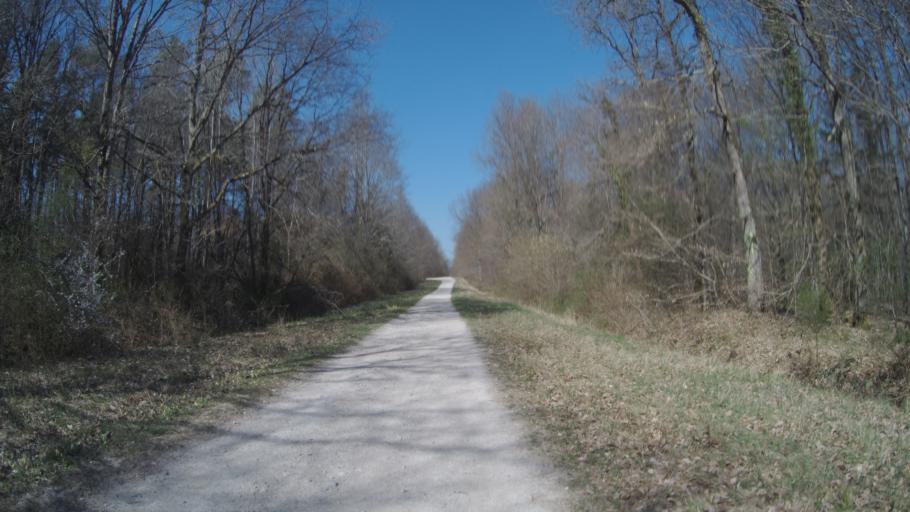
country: FR
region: Centre
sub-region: Departement du Loiret
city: Chanteau
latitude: 47.9519
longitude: 1.9820
